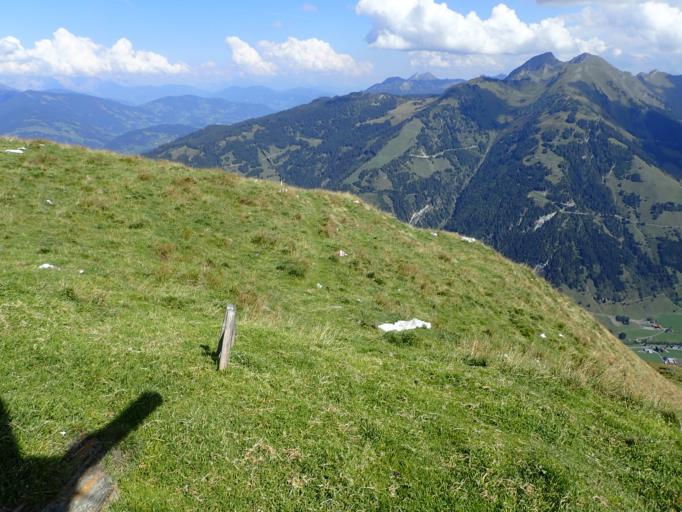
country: AT
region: Salzburg
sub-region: Politischer Bezirk Zell am See
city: Taxenbach
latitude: 47.2457
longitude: 12.9582
